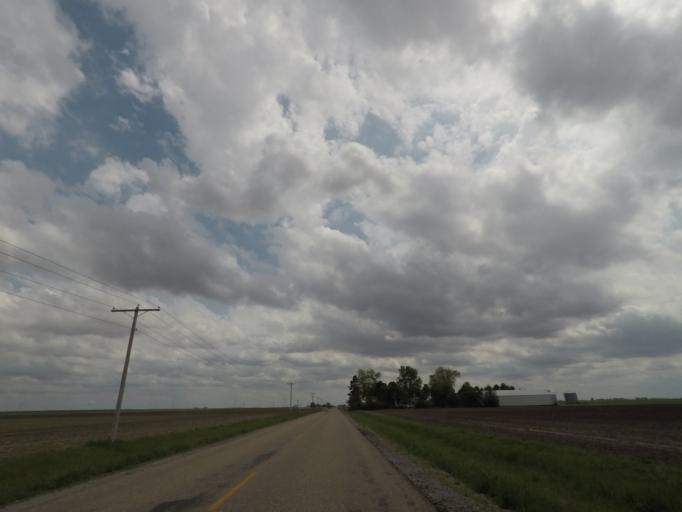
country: US
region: Illinois
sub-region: Macon County
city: Maroa
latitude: 40.0835
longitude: -89.0859
